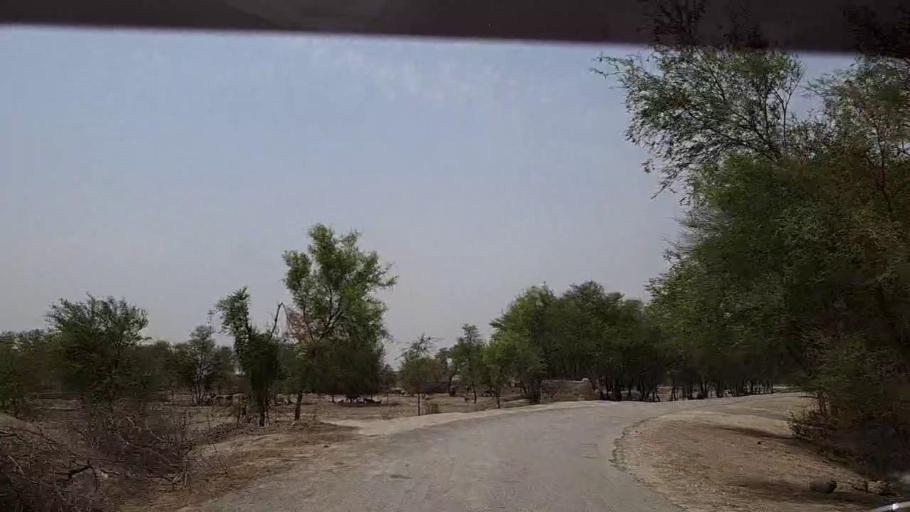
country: PK
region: Sindh
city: Khairpur Nathan Shah
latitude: 27.0172
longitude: 67.5932
